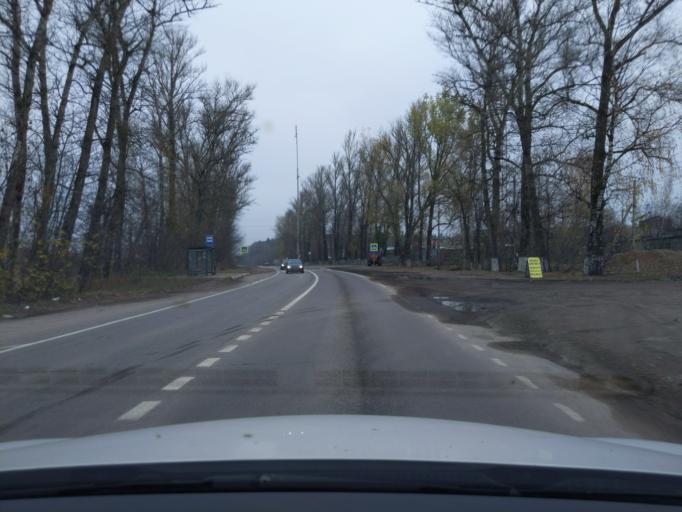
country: RU
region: Moskovskaya
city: Ashukino
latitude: 56.1404
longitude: 37.9880
